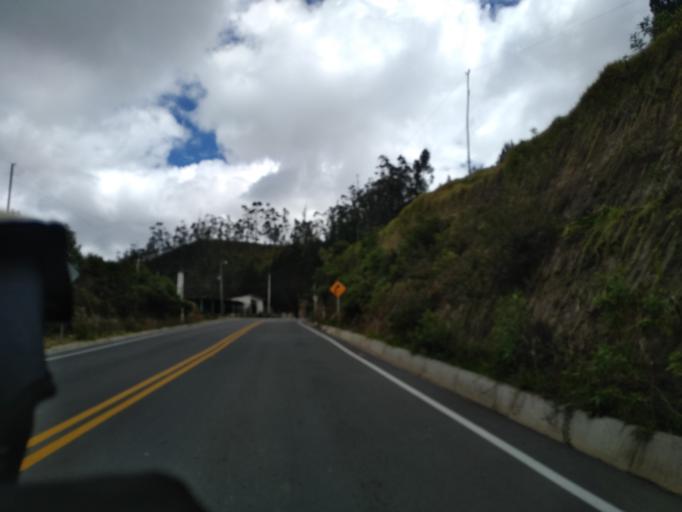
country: EC
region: Cotopaxi
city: Saquisili
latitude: -0.7761
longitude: -78.9088
